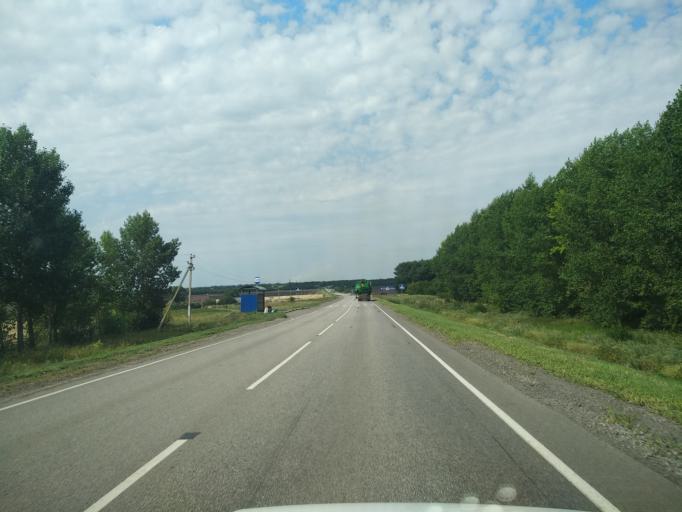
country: RU
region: Lipetsk
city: Dobrinka
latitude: 51.8874
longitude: 40.4319
